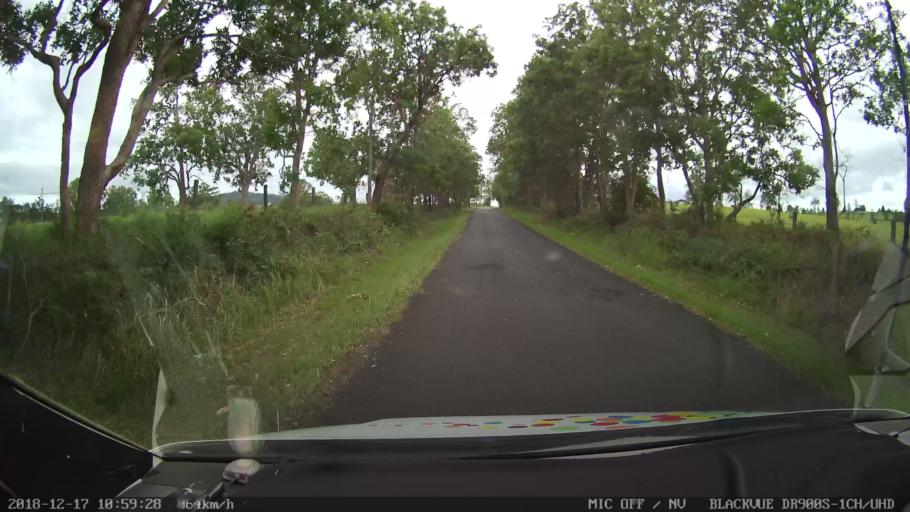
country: AU
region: New South Wales
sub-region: Richmond Valley
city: Casino
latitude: -28.8203
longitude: 152.6116
